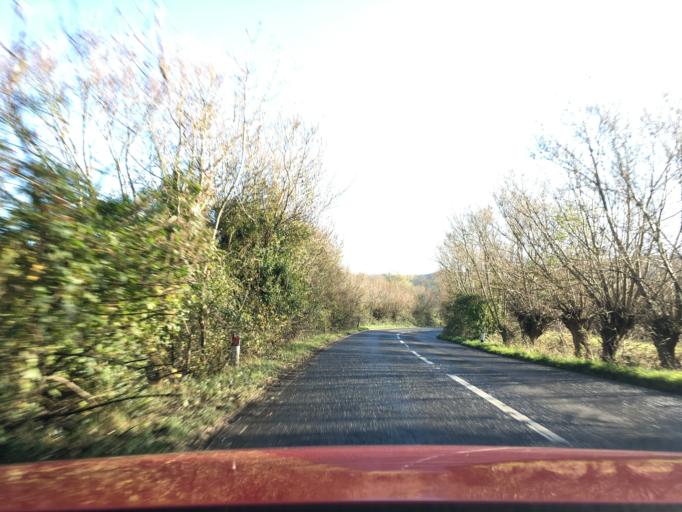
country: GB
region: England
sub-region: Somerset
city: Langport
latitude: 51.0781
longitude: -2.8587
